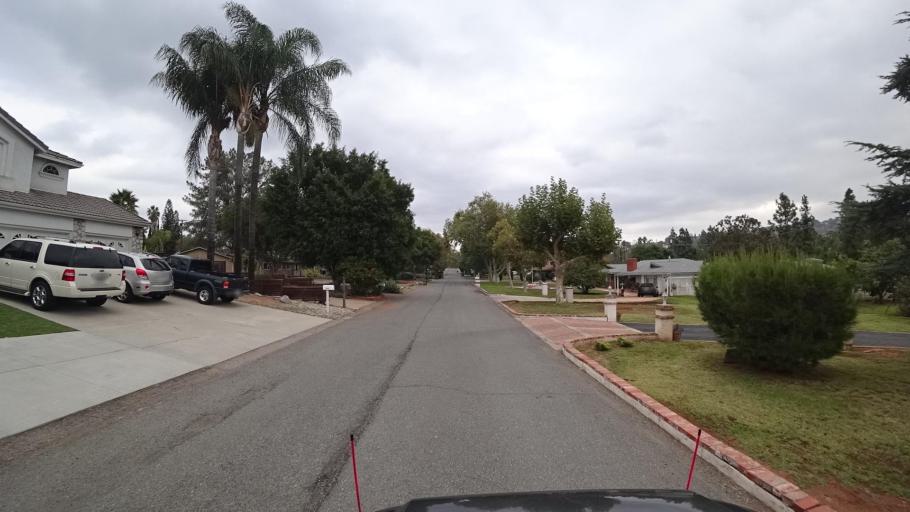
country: US
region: California
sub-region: San Diego County
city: Spring Valley
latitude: 32.7466
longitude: -116.9950
